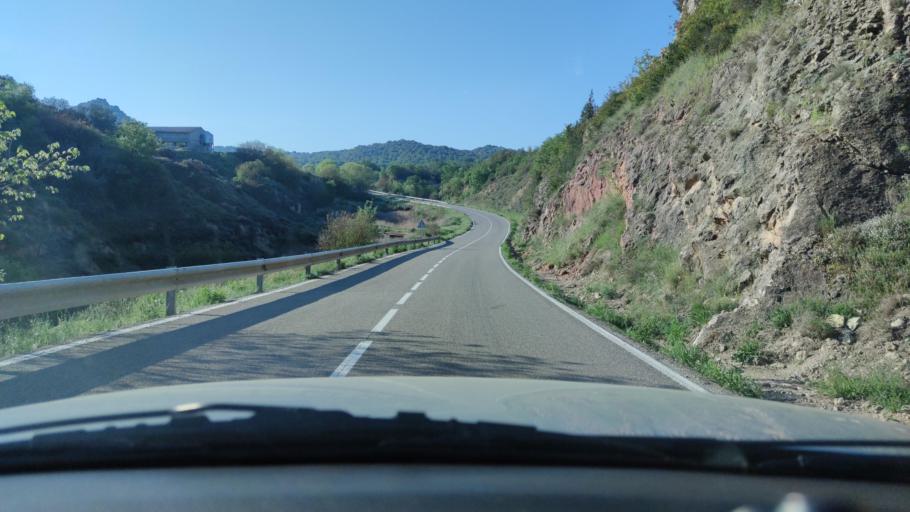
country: ES
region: Catalonia
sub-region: Provincia de Lleida
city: Artesa de Segre
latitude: 41.8860
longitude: 0.9975
